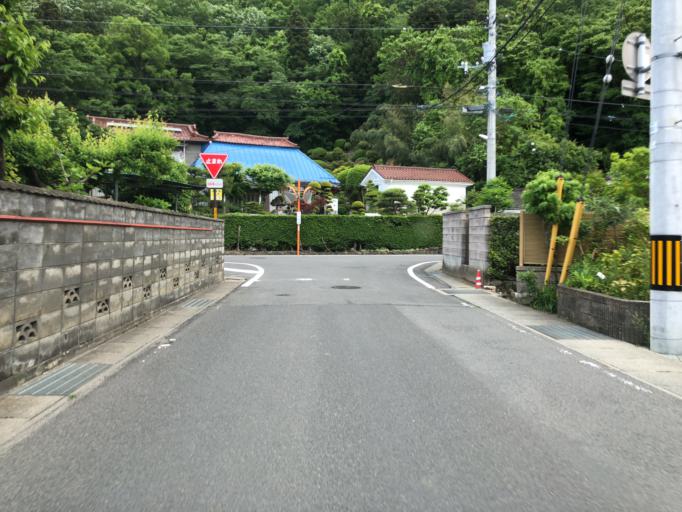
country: JP
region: Fukushima
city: Fukushima-shi
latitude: 37.7740
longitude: 140.4600
